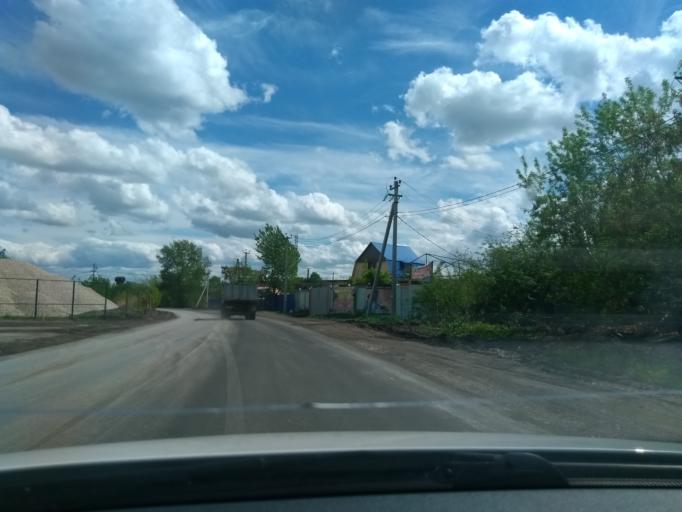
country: RU
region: Perm
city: Kondratovo
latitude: 58.0112
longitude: 56.0643
